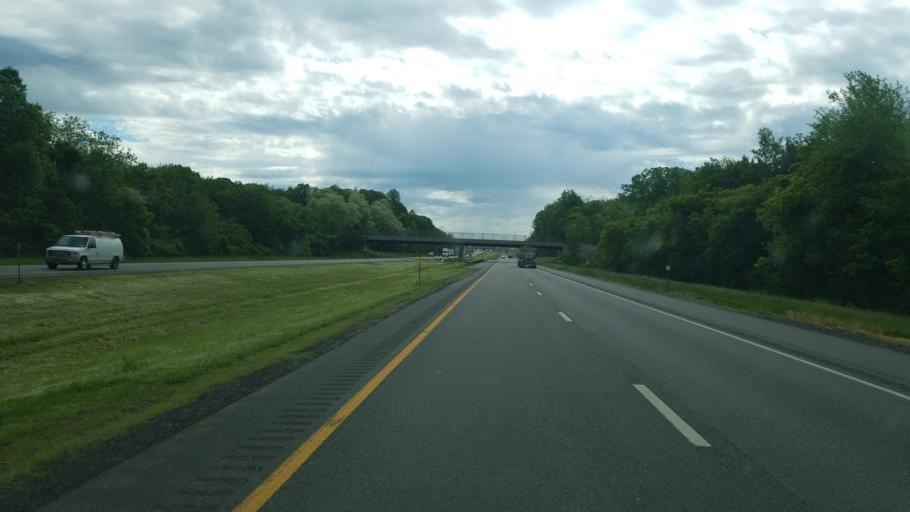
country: US
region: New York
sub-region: Seneca County
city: Waterloo
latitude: 42.9593
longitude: -76.9396
